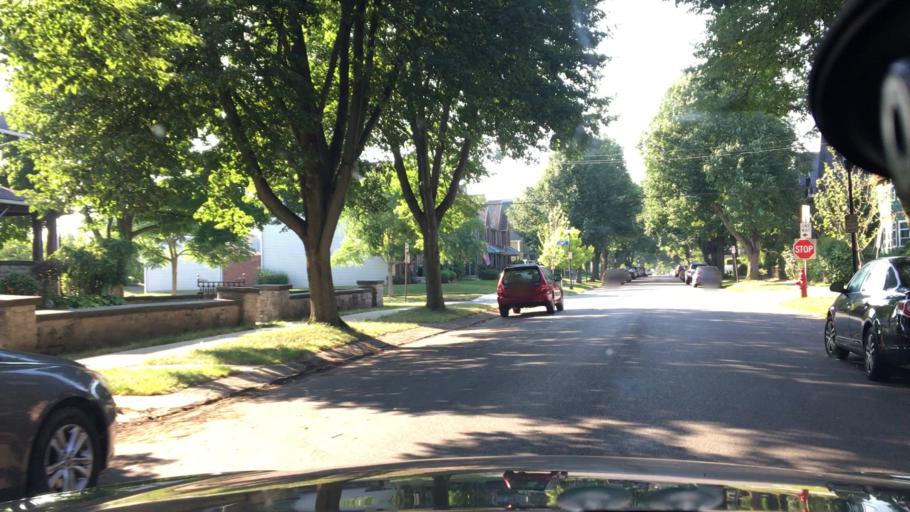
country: US
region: New York
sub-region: Erie County
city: Buffalo
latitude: 42.9035
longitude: -78.8960
